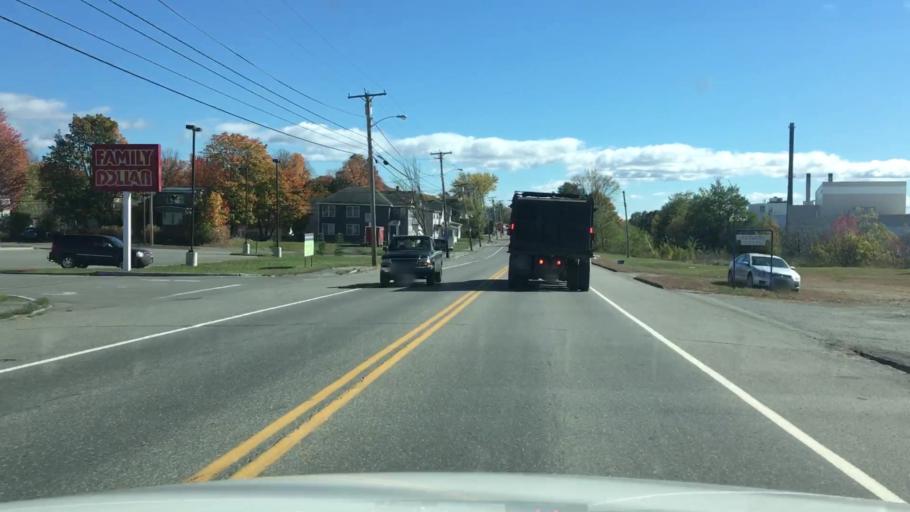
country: US
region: Maine
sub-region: Penobscot County
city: East Millinocket
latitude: 45.6273
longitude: -68.5816
